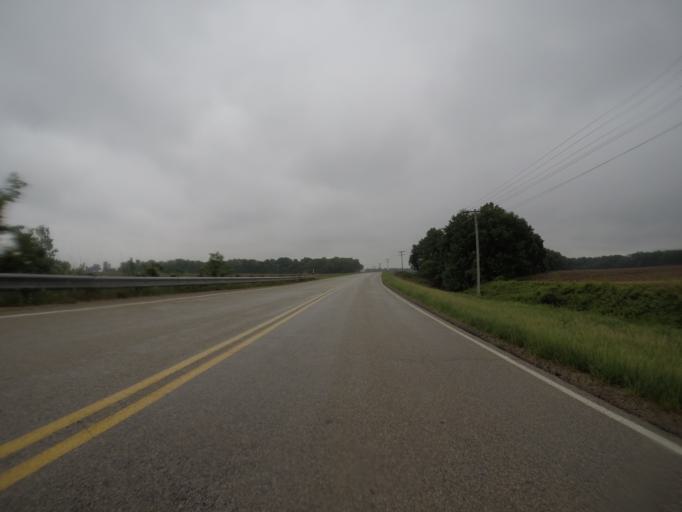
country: US
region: Kansas
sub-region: Pottawatomie County
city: Wamego
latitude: 39.2354
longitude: -96.2313
